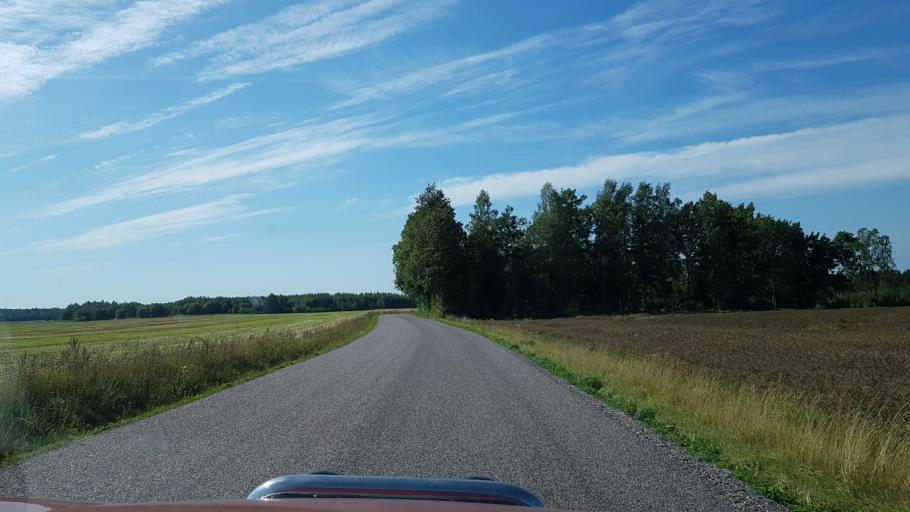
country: EE
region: Tartu
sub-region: Puhja vald
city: Puhja
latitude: 58.2544
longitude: 26.2856
